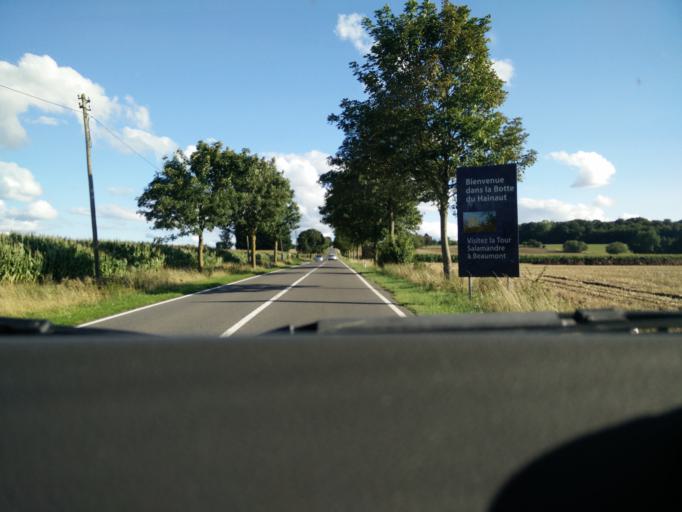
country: BE
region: Wallonia
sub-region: Province du Hainaut
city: Beaumont
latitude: 50.2699
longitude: 4.2140
